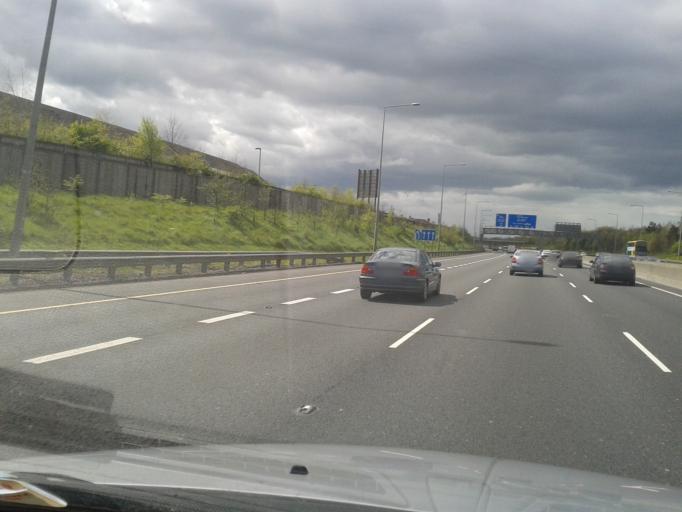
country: IE
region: Leinster
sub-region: Dublin City
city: Finglas
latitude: 53.4078
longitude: -6.2916
